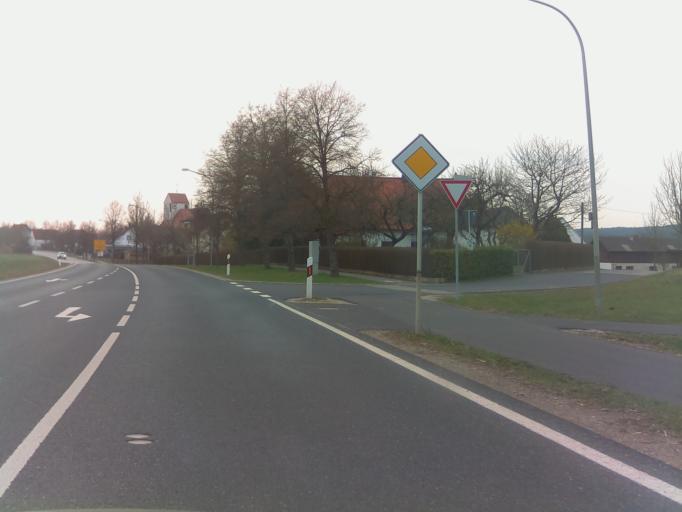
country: DE
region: Bavaria
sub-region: Upper Palatinate
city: Schmidgaden
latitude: 49.4382
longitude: 12.0523
